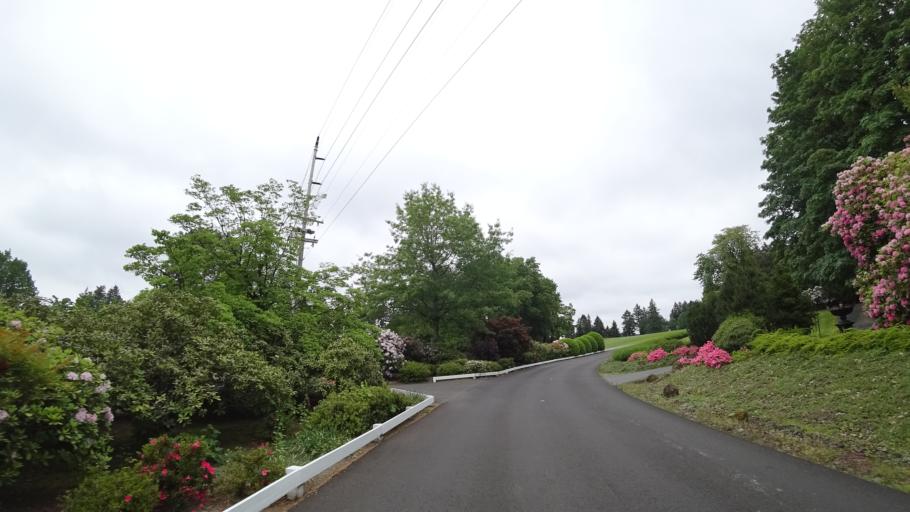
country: US
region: Oregon
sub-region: Clackamas County
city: Milwaukie
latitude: 45.4523
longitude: -122.6523
